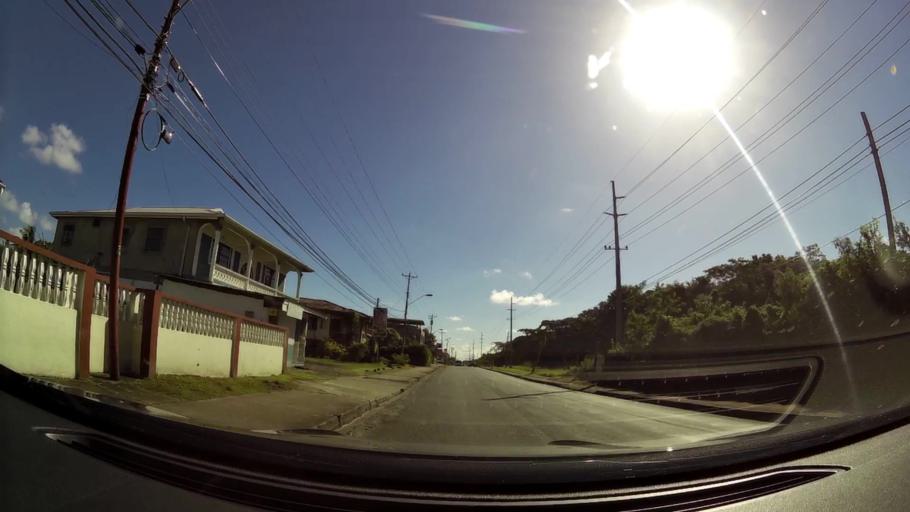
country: TT
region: Tobago
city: Scarborough
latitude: 11.1566
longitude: -60.8097
